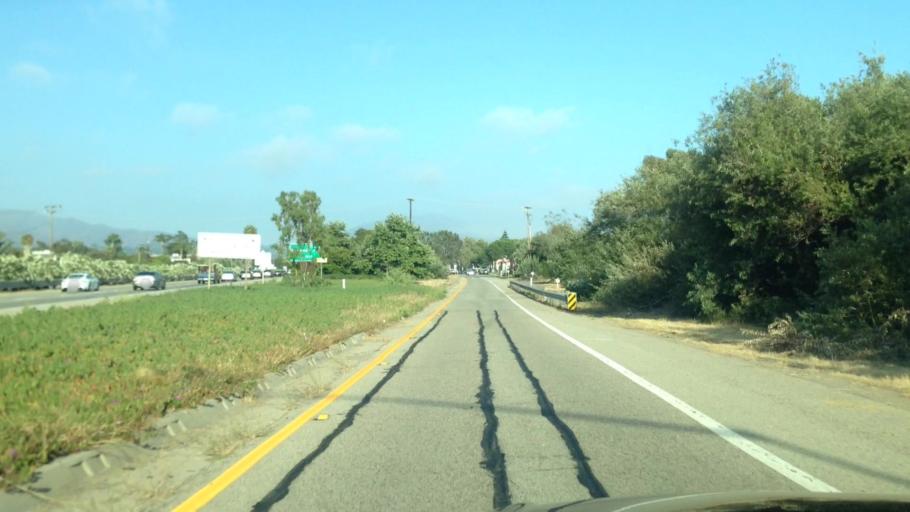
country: US
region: California
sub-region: Santa Barbara County
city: Carpinteria
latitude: 34.4052
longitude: -119.5377
